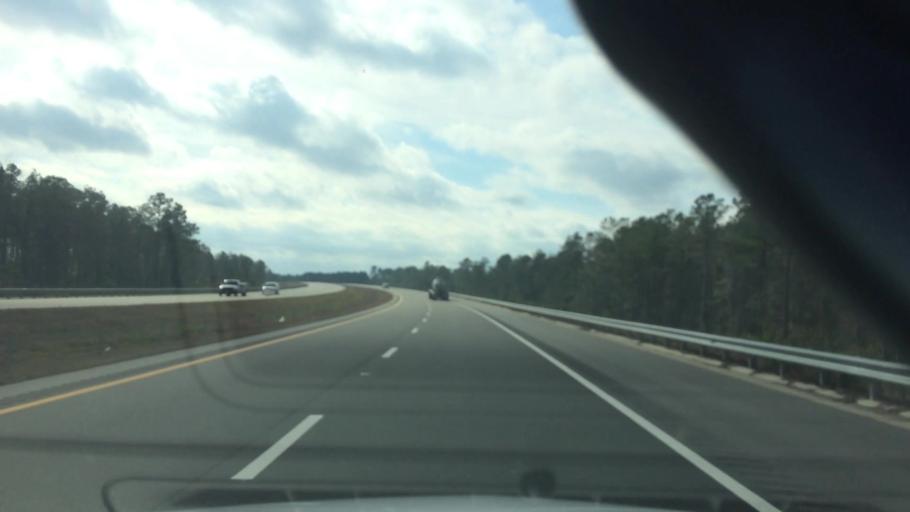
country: US
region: North Carolina
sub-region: Brunswick County
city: Leland
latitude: 34.2764
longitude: -78.0715
